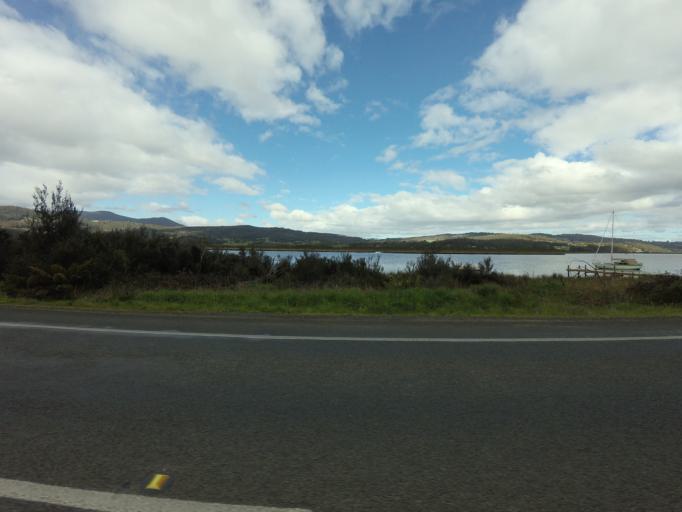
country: AU
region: Tasmania
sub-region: Huon Valley
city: Franklin
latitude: -43.1030
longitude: 147.0020
